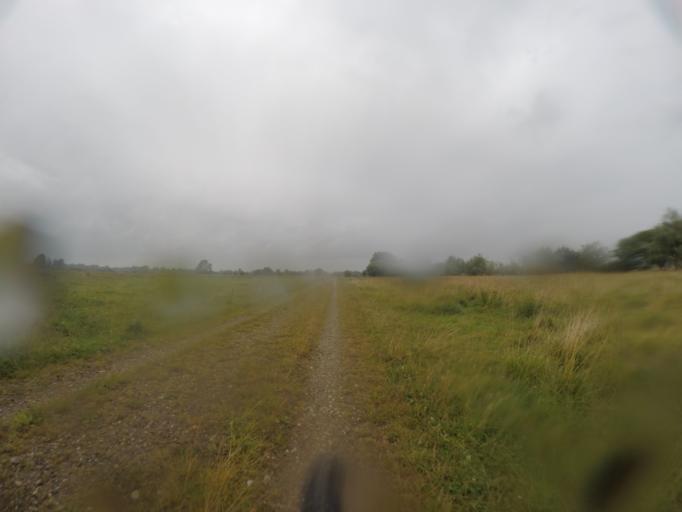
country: DK
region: Capital Region
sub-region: Hoje-Taastrup Kommune
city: Taastrup
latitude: 55.6922
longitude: 12.3113
